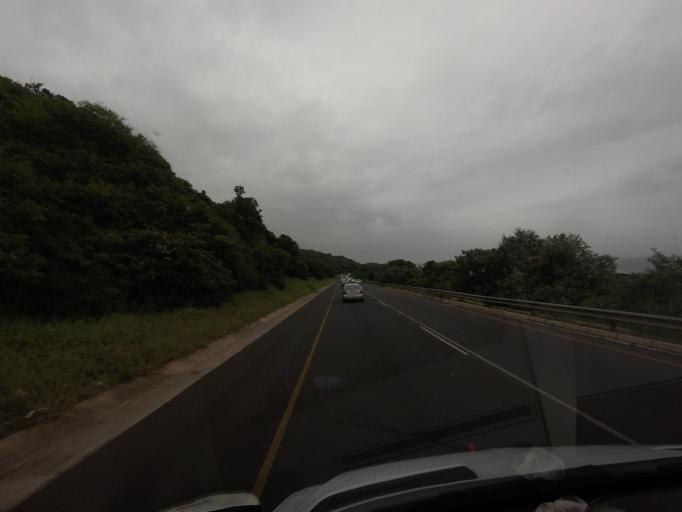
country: ZA
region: KwaZulu-Natal
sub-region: eThekwini Metropolitan Municipality
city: Durban
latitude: -29.7129
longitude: 31.0908
